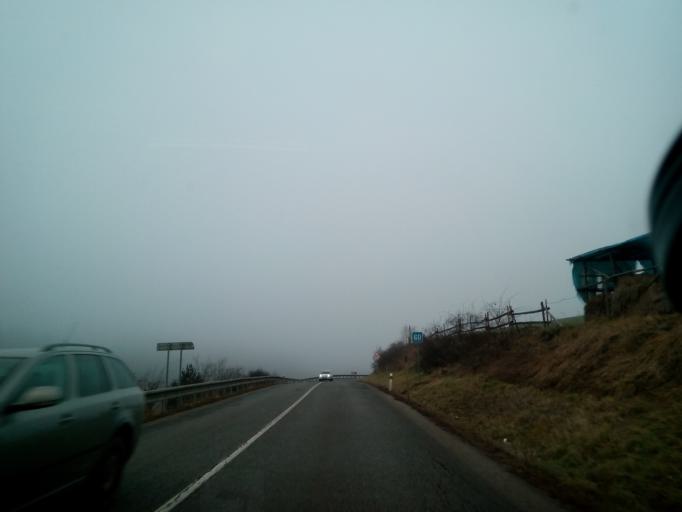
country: SK
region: Kosicky
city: Krompachy
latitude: 48.9296
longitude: 20.8438
